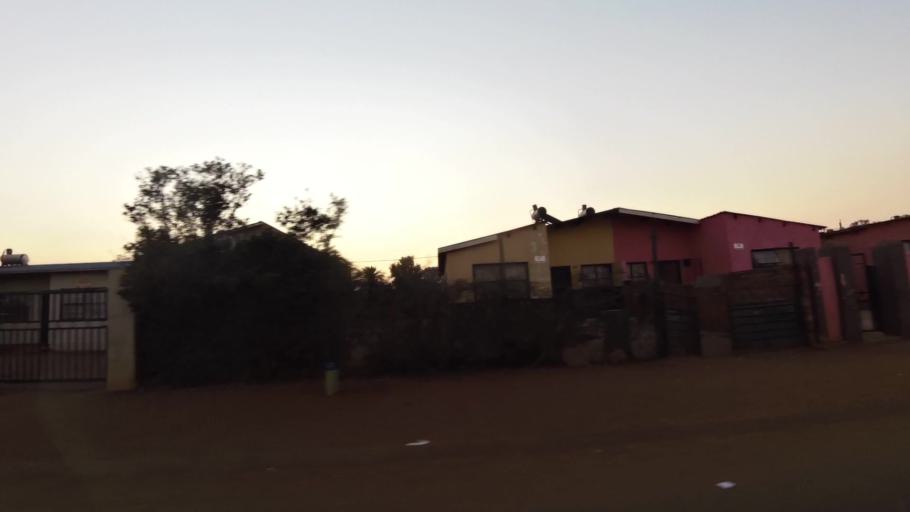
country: ZA
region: Gauteng
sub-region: City of Johannesburg Metropolitan Municipality
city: Soweto
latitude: -26.2901
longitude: 27.8739
